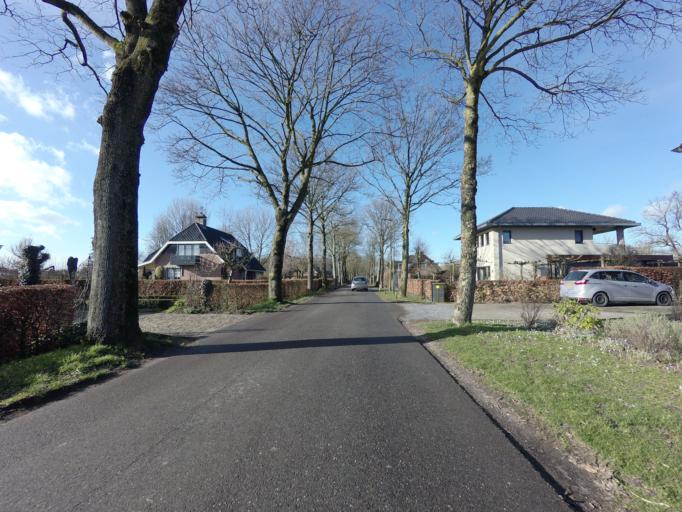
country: NL
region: Utrecht
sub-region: Gemeente Montfoort
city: Montfoort
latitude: 52.0978
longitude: 4.9625
